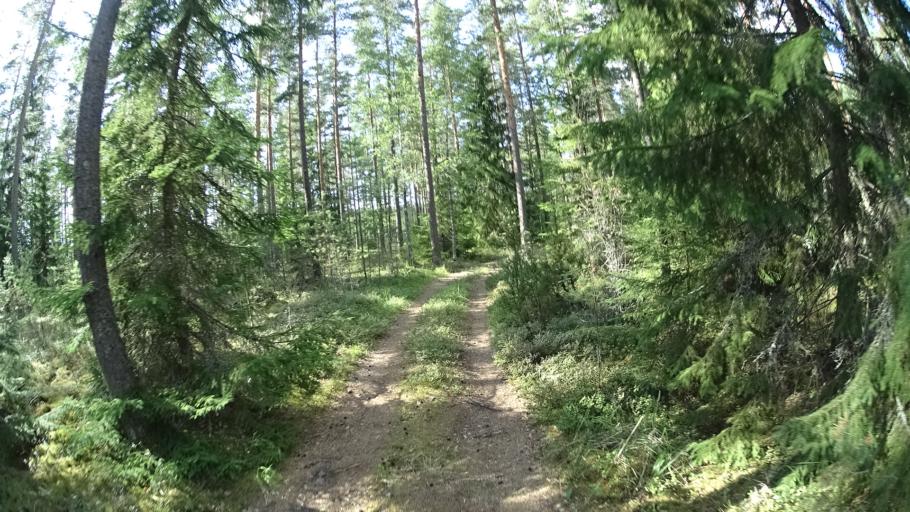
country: FI
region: Uusimaa
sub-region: Helsinki
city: Kaerkoelae
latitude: 60.7346
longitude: 24.0577
